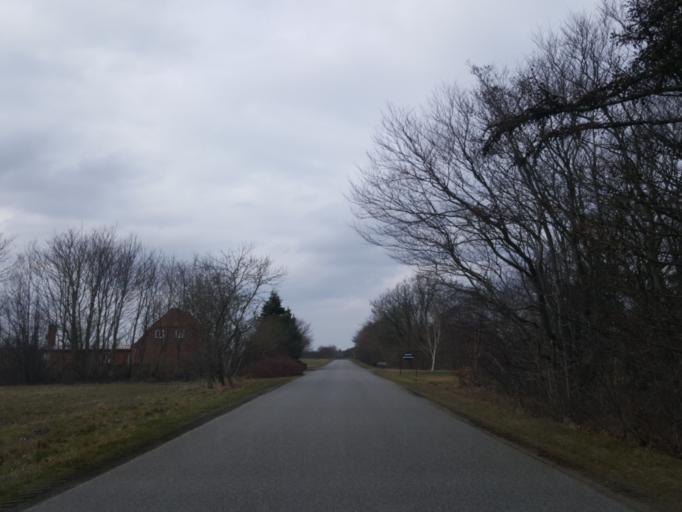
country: DK
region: Central Jutland
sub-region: Holstebro Kommune
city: Ulfborg
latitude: 56.3644
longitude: 8.2481
